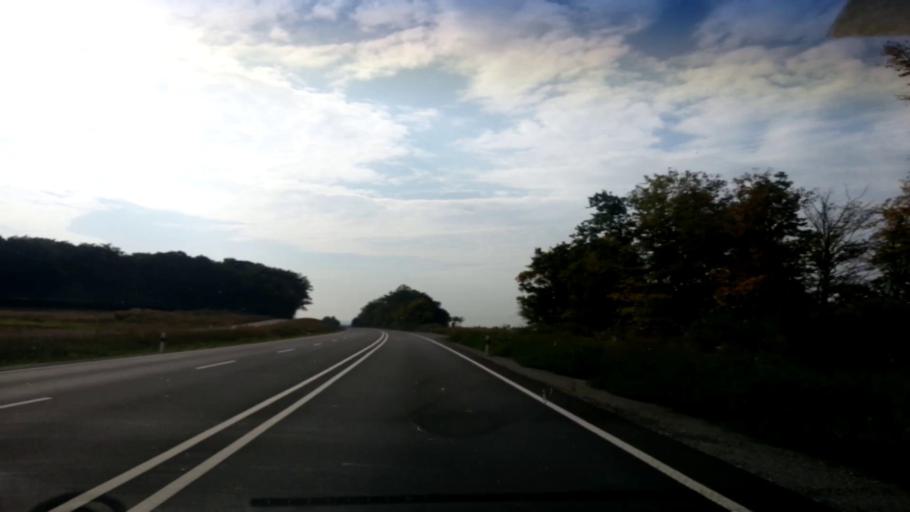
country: DE
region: Bavaria
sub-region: Regierungsbezirk Unterfranken
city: Gerolzhofen
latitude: 49.8838
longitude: 10.3563
